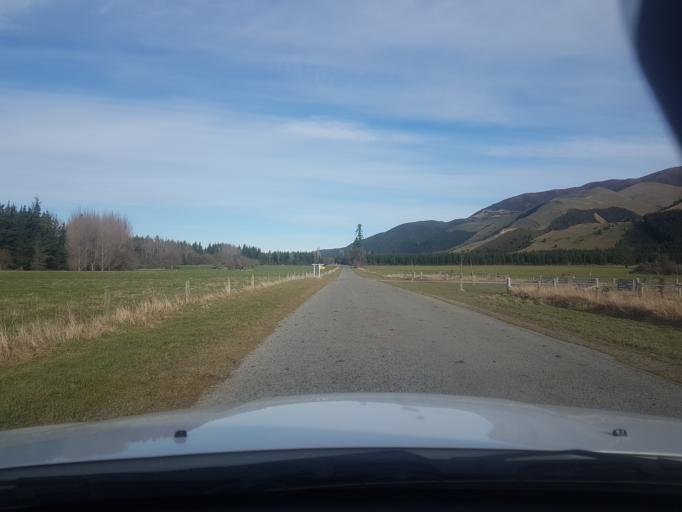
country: NZ
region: Canterbury
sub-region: Timaru District
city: Pleasant Point
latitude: -43.8418
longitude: 171.2540
